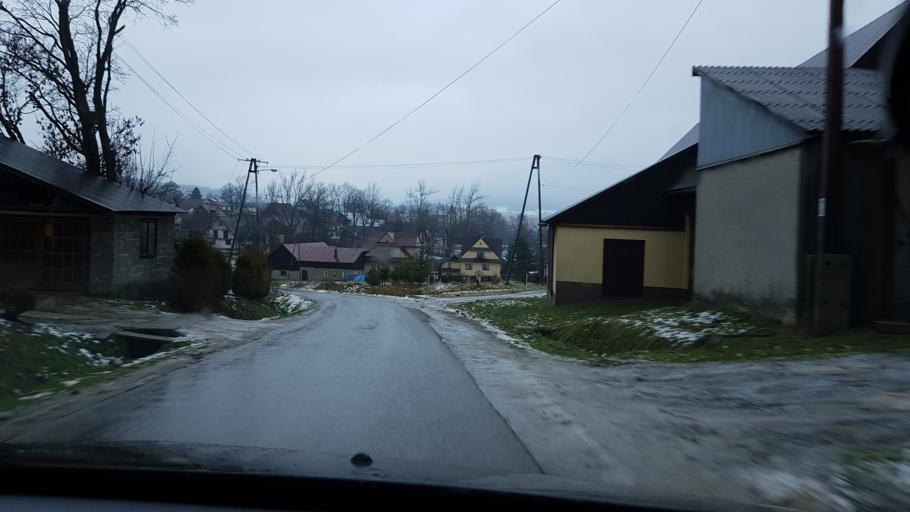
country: PL
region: Lesser Poland Voivodeship
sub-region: Powiat nowotarski
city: Lasek
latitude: 49.4918
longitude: 19.9365
